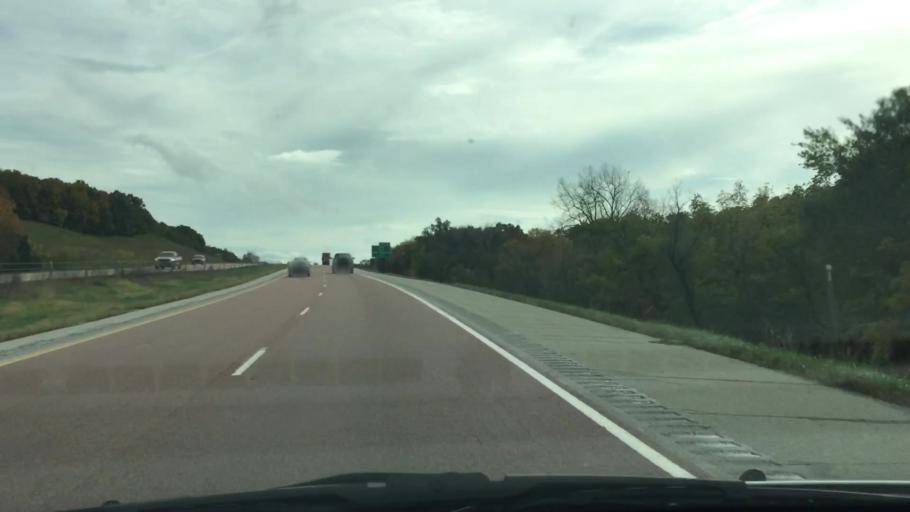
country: US
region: Iowa
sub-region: Clarke County
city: Osceola
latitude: 41.1974
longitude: -93.7874
